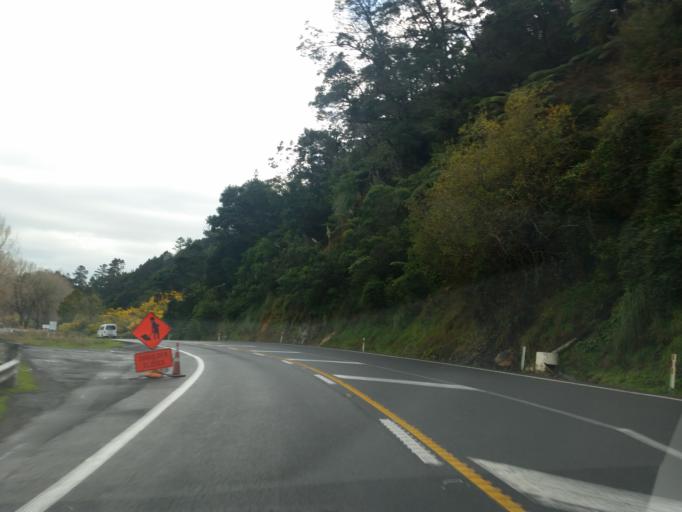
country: NZ
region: Waikato
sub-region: Hauraki District
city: Paeroa
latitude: -37.4180
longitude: 175.7186
